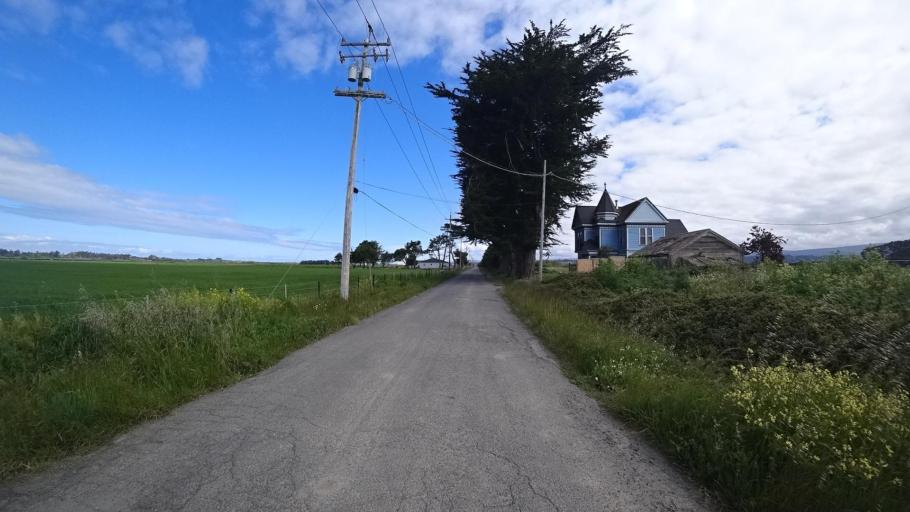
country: US
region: California
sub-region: Humboldt County
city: Arcata
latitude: 40.8871
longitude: -124.1156
